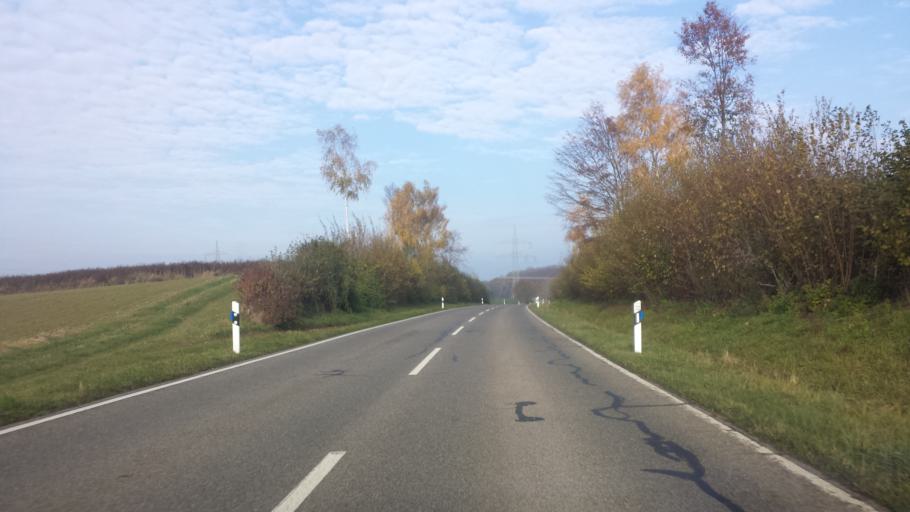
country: DE
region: Baden-Wuerttemberg
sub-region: Karlsruhe Region
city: Huffenhardt
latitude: 49.3046
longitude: 9.0794
